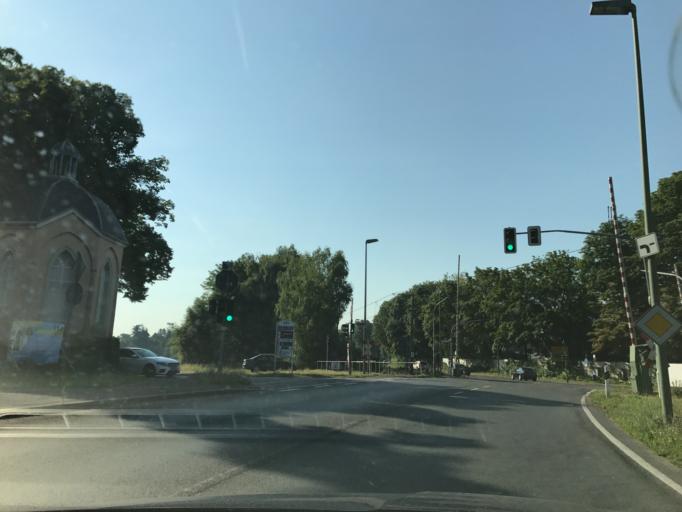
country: DE
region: North Rhine-Westphalia
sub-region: Regierungsbezirk Dusseldorf
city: Meerbusch
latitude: 51.2658
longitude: 6.6722
